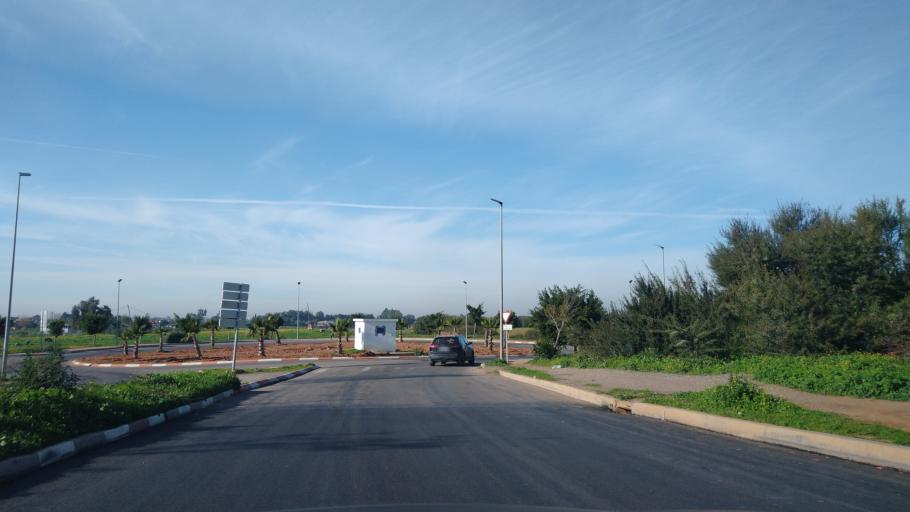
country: MA
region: Rabat-Sale-Zemmour-Zaer
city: Sale
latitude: 33.9997
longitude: -6.7503
